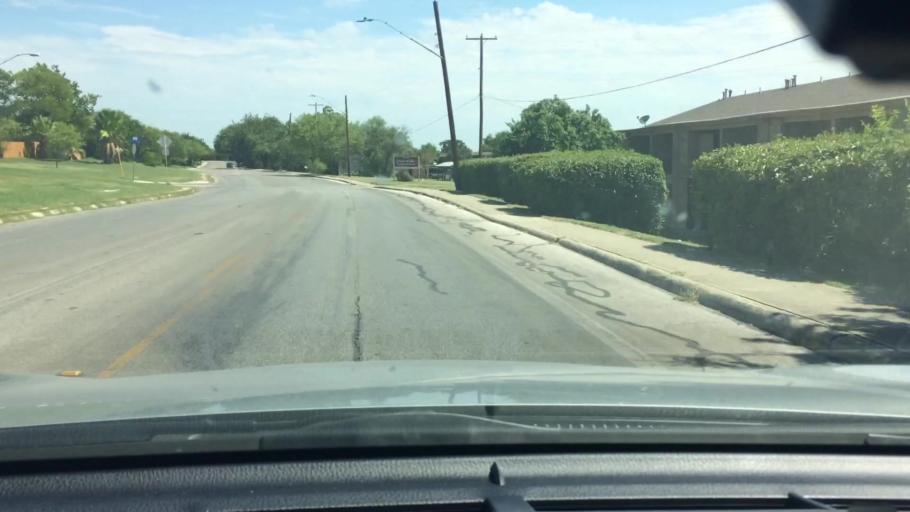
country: US
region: Texas
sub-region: Bexar County
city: San Antonio
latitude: 29.3784
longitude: -98.4318
